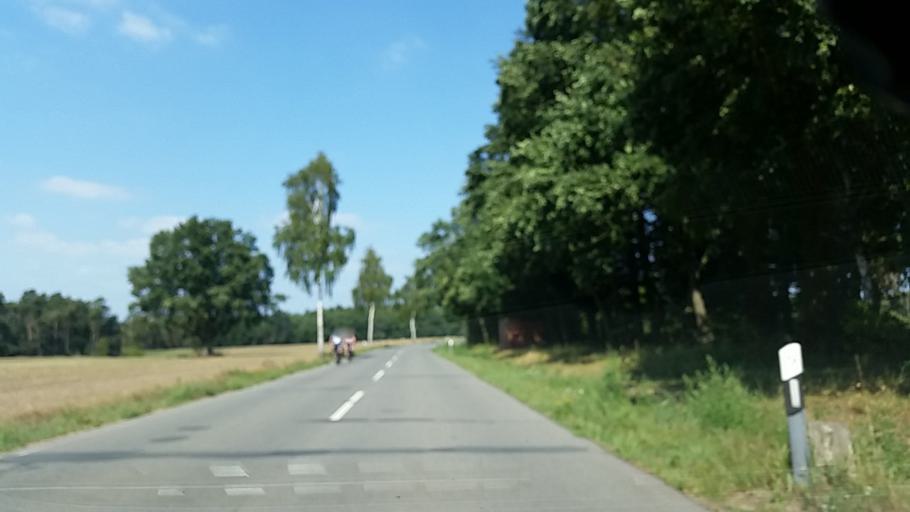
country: DE
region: Lower Saxony
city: Jelmstorf
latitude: 53.1270
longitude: 10.5326
